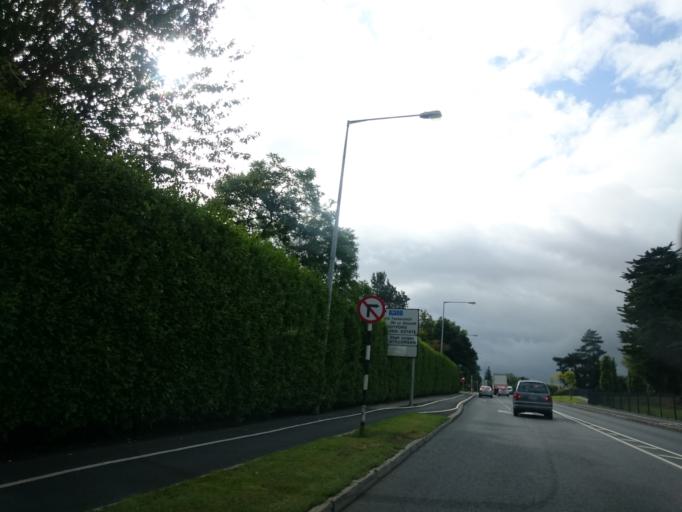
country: IE
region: Leinster
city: Sandyford
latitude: 53.2900
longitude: -6.2272
